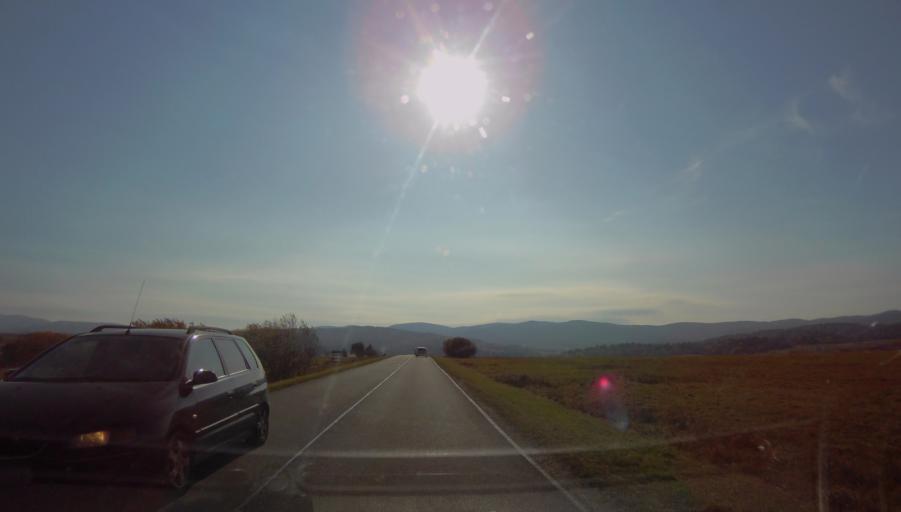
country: PL
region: Subcarpathian Voivodeship
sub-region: Powiat sanocki
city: Komancza
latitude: 49.2553
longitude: 22.0961
